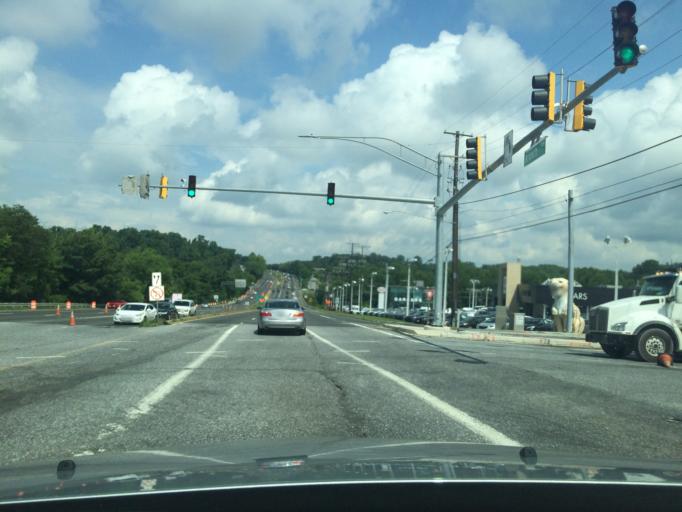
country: US
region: Maryland
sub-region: Prince George's County
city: Suitland
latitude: 38.8255
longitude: -76.9243
